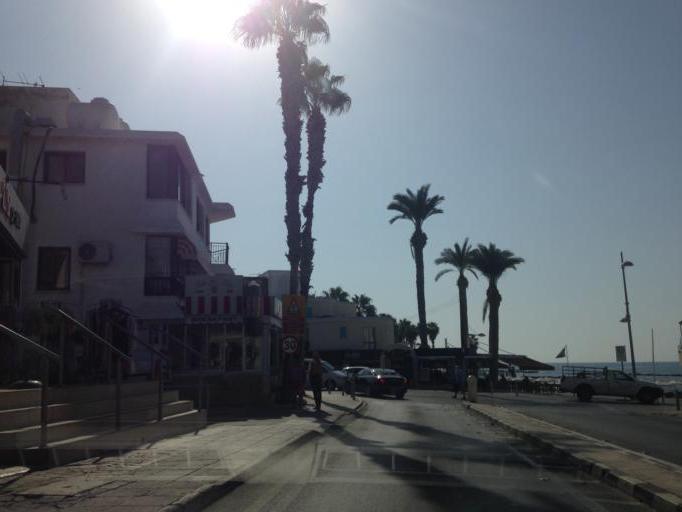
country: CY
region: Pafos
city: Paphos
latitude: 34.7564
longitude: 32.4154
